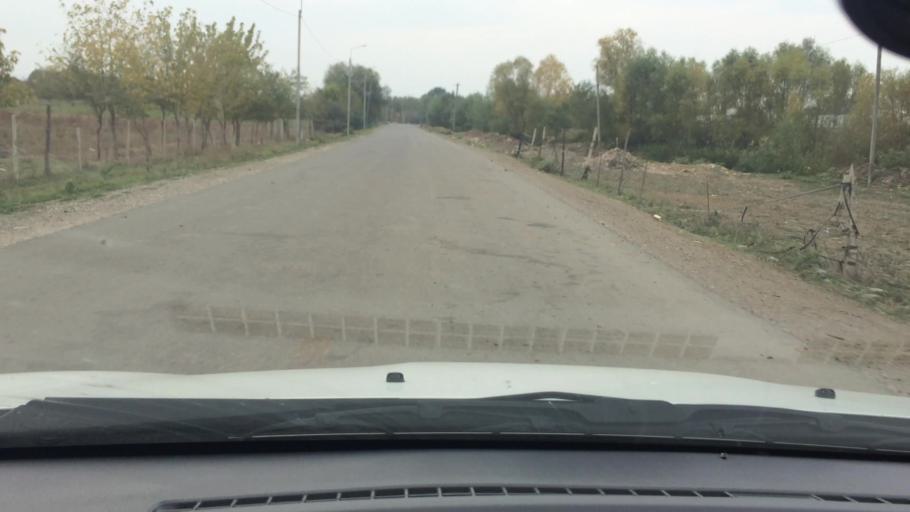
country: AM
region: Tavush
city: Berdavan
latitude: 41.3483
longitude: 44.9765
